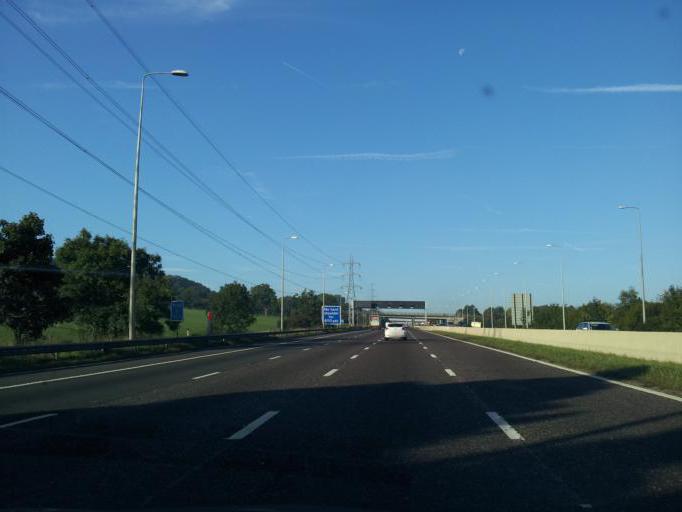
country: GB
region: England
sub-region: Calderdale
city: Brighouse
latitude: 53.6840
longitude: -1.7754
